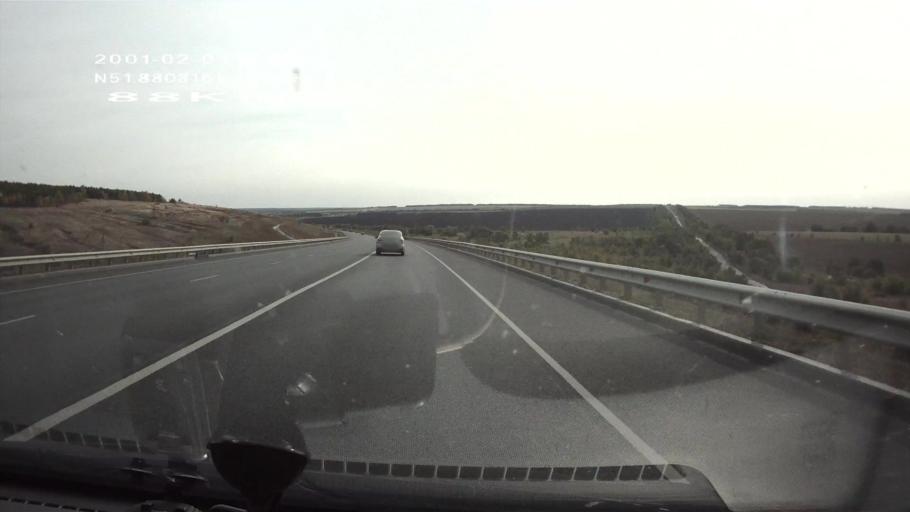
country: RU
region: Saratov
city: Yelshanka
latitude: 51.8804
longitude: 46.5099
